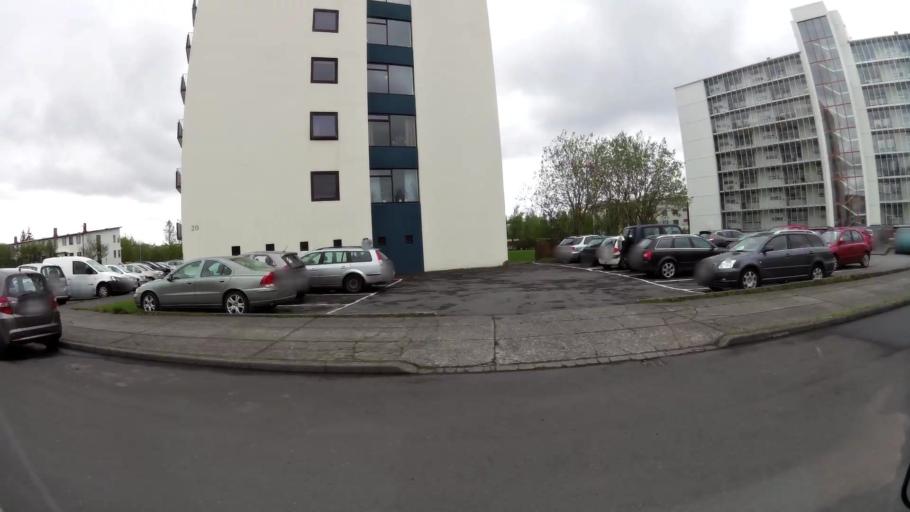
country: IS
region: Capital Region
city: Reykjavik
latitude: 64.1325
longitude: -21.8623
